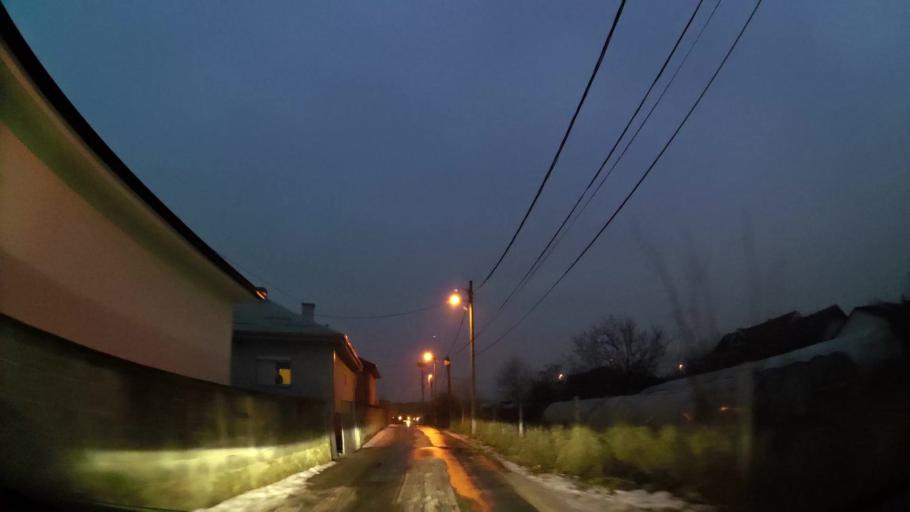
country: MK
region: Kisela Voda
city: Kisela Voda
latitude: 41.9706
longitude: 21.4858
